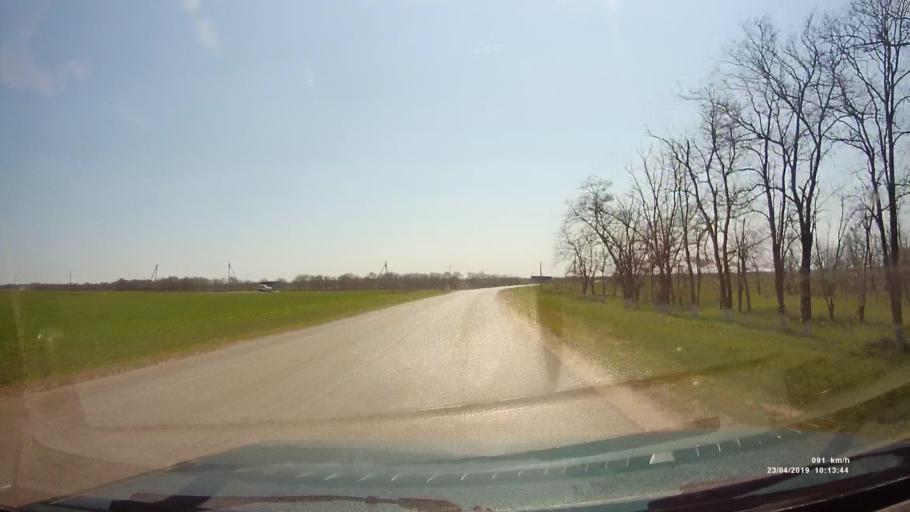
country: RU
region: Rostov
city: Sovetskoye
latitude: 46.6830
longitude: 42.3610
